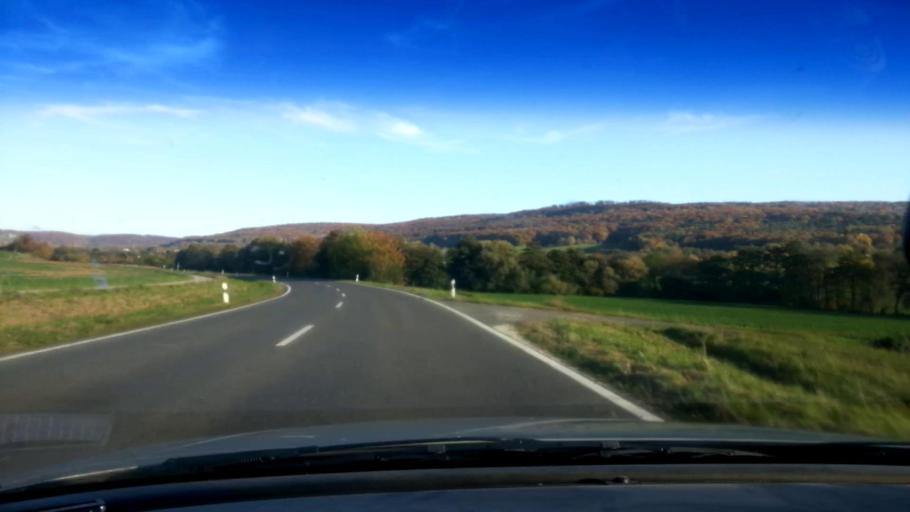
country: DE
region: Bavaria
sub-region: Upper Franconia
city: Litzendorf
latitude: 49.9155
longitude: 11.0279
